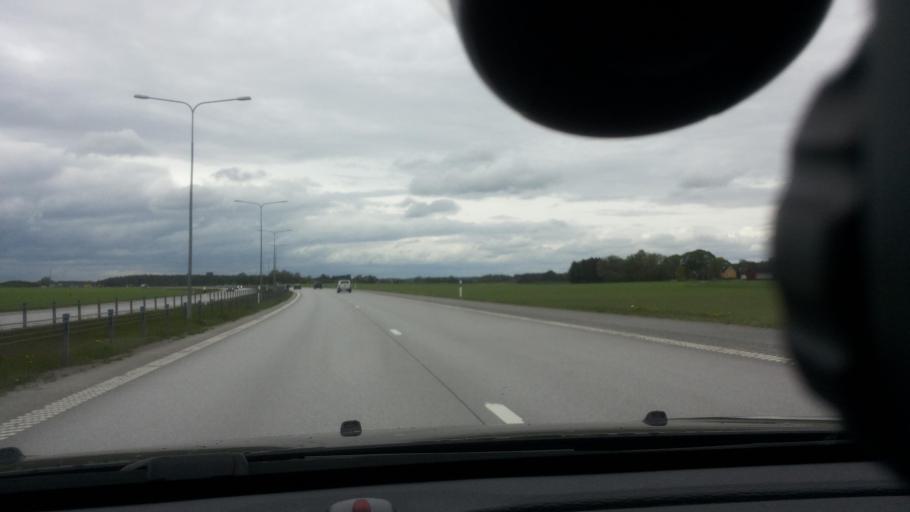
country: SE
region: Uppsala
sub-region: Uppsala Kommun
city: Saevja
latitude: 59.8537
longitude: 17.7326
